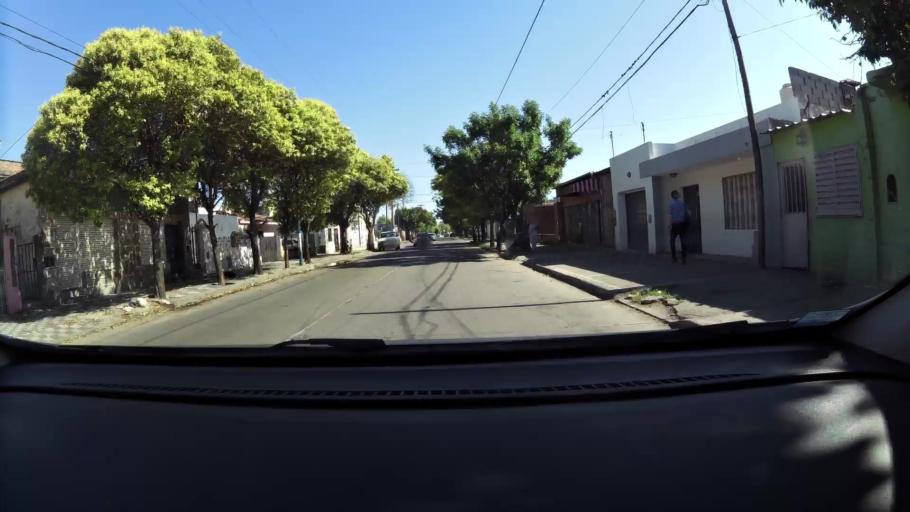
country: AR
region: Cordoba
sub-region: Departamento de Capital
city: Cordoba
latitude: -31.4372
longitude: -64.1486
